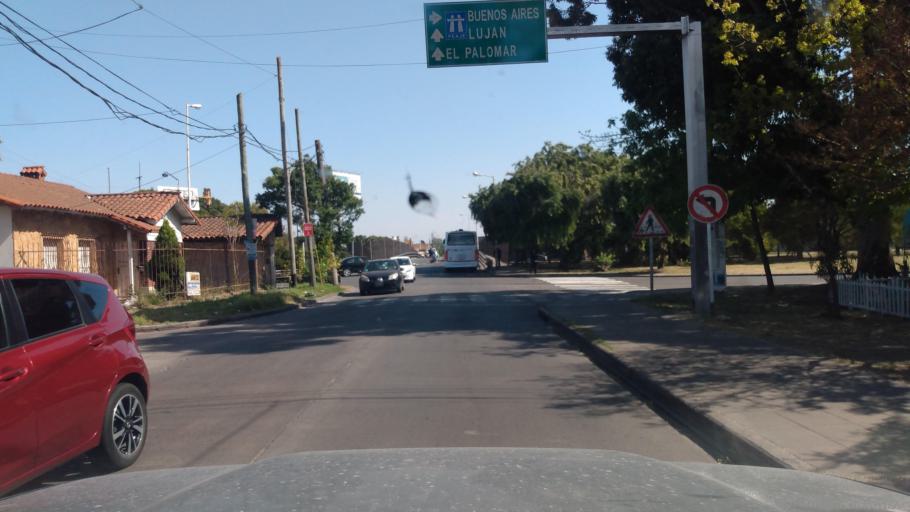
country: AR
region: Buenos Aires
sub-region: Partido de Moron
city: Moron
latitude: -34.6331
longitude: -58.5994
